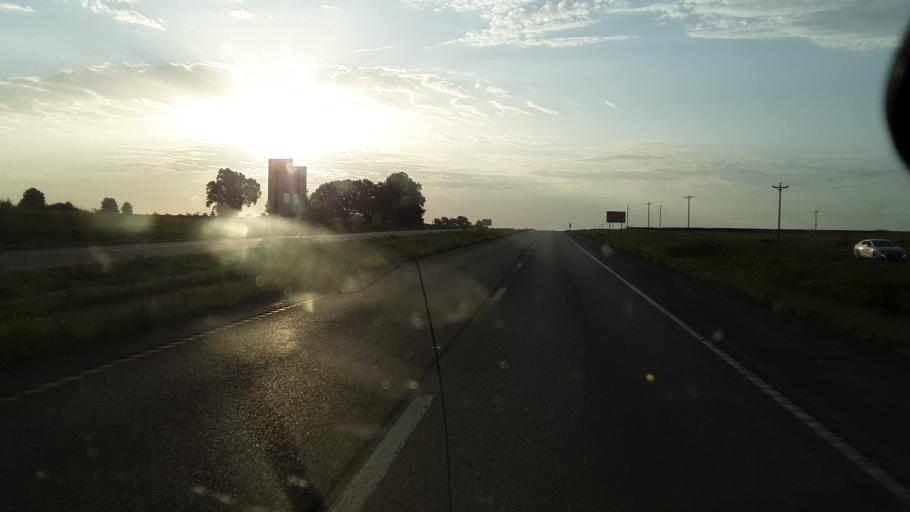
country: US
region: Missouri
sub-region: Callaway County
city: Fulton
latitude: 38.9438
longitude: -91.9229
